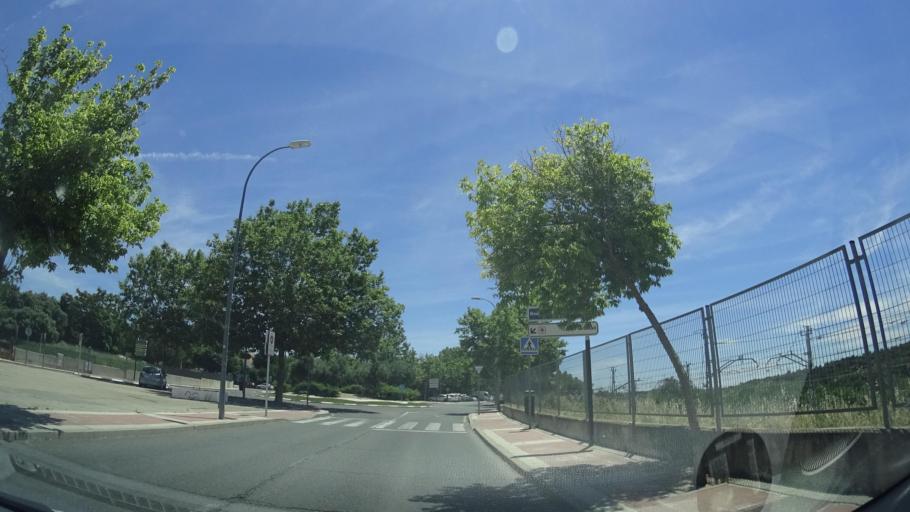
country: ES
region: Madrid
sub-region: Provincia de Madrid
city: Collado-Villalba
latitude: 40.6251
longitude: -4.0009
